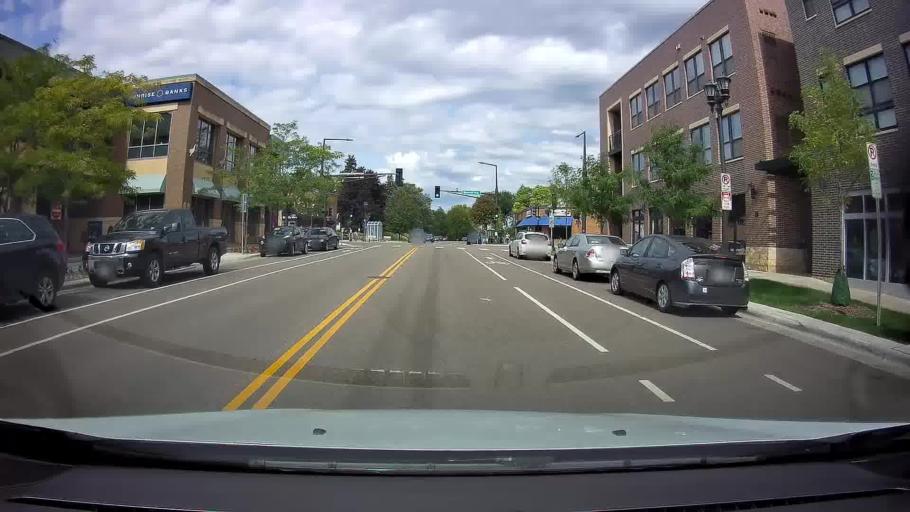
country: US
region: Minnesota
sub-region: Ramsey County
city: Lauderdale
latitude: 44.9820
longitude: -93.1953
